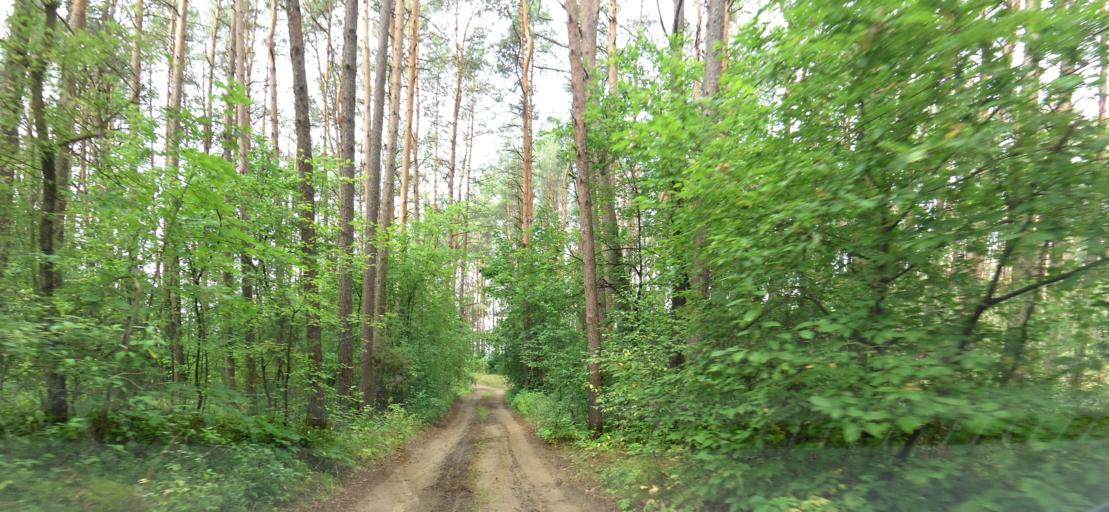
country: LT
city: Trakai
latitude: 54.5065
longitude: 24.9798
